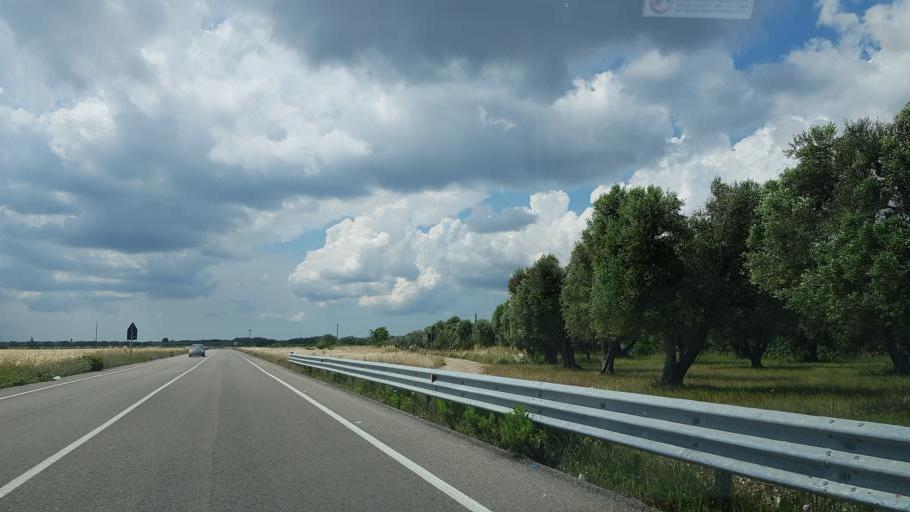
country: IT
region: Apulia
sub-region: Provincia di Brindisi
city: Mesagne
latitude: 40.5042
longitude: 17.8278
